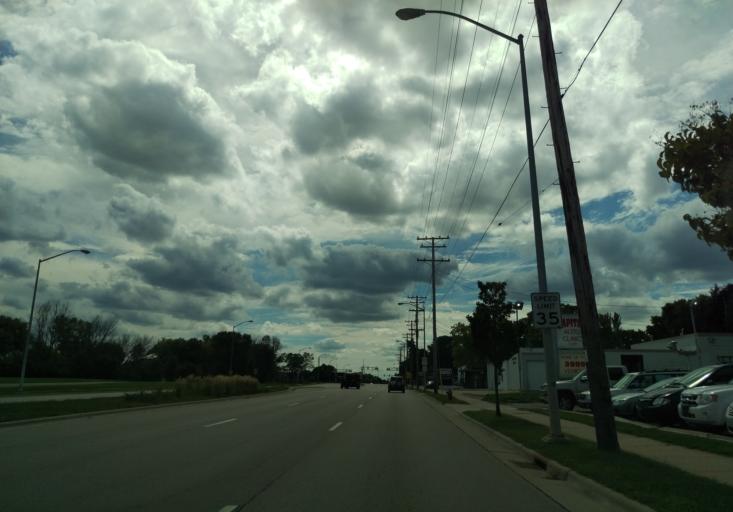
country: US
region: Wisconsin
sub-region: Dane County
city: Maple Bluff
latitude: 43.1250
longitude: -89.3553
